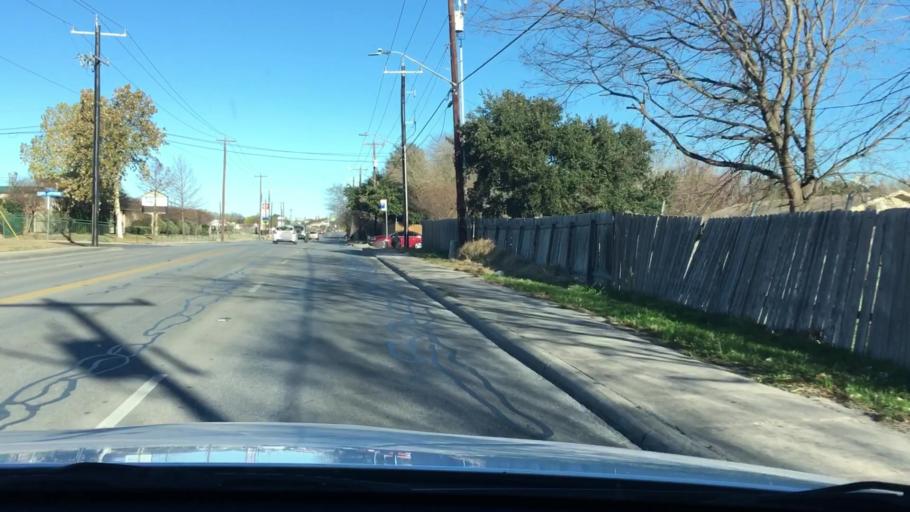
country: US
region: Texas
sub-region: Bexar County
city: Live Oak
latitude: 29.5768
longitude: -98.3900
